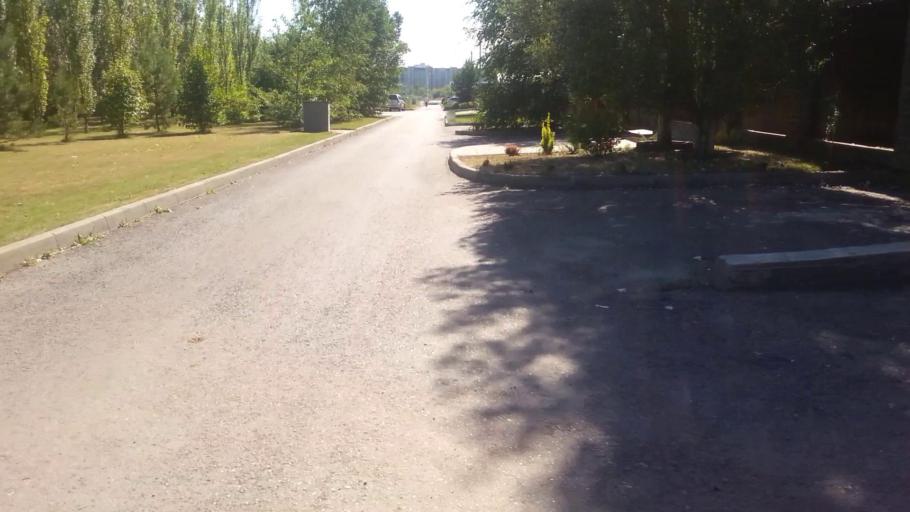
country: RU
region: Altai Krai
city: Novosilikatnyy
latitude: 53.3531
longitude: 83.6546
